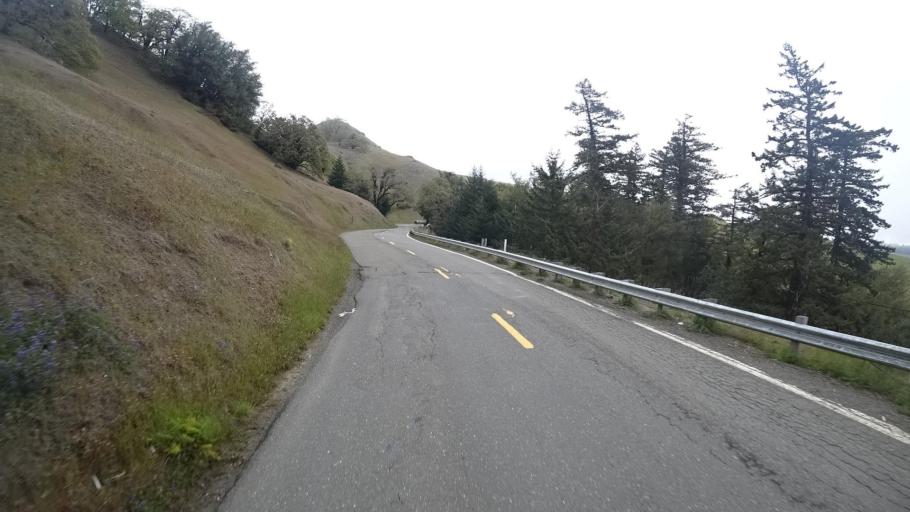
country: US
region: California
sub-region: Humboldt County
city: Redway
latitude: 40.1045
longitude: -123.6950
